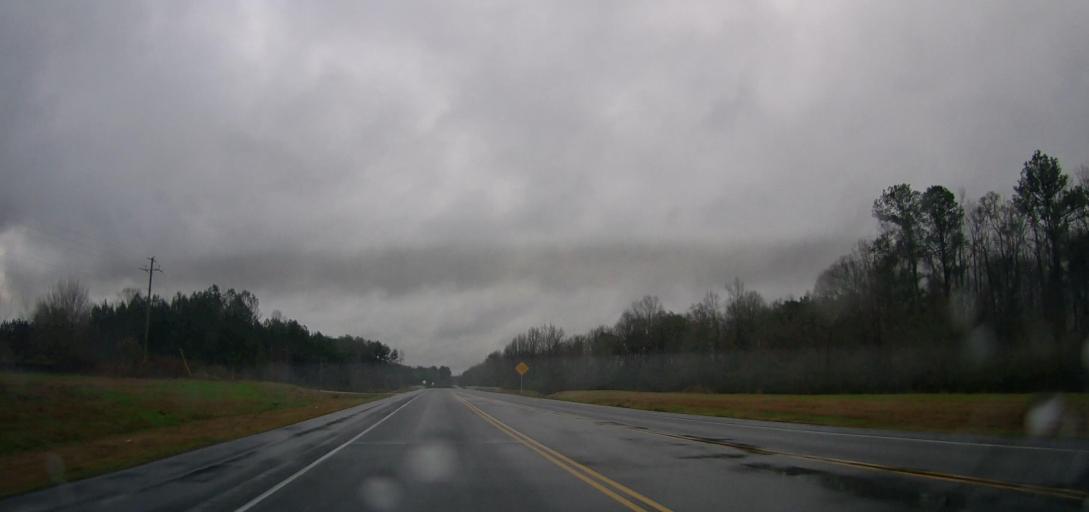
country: US
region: Alabama
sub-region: Bibb County
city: Centreville
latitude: 32.9327
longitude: -87.0583
